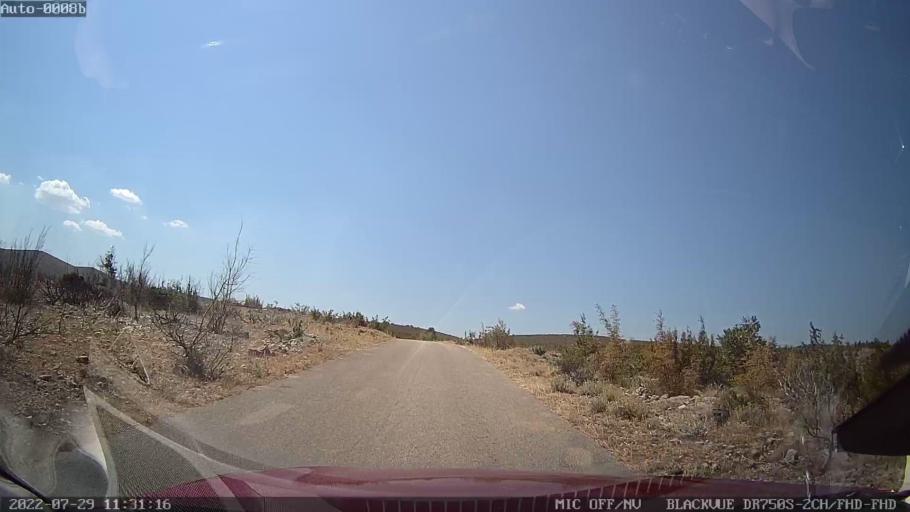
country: HR
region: Zadarska
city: Obrovac
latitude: 44.1987
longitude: 15.7468
